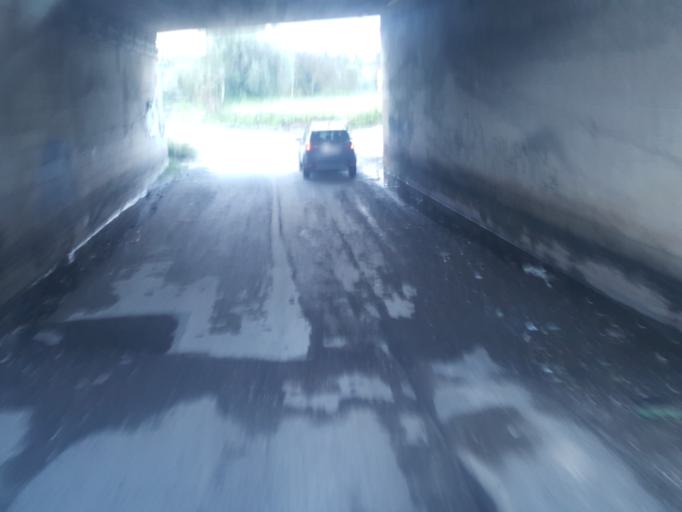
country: IT
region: Sicily
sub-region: Catania
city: Belvedere-Piano Tavola
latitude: 37.5387
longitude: 14.9674
